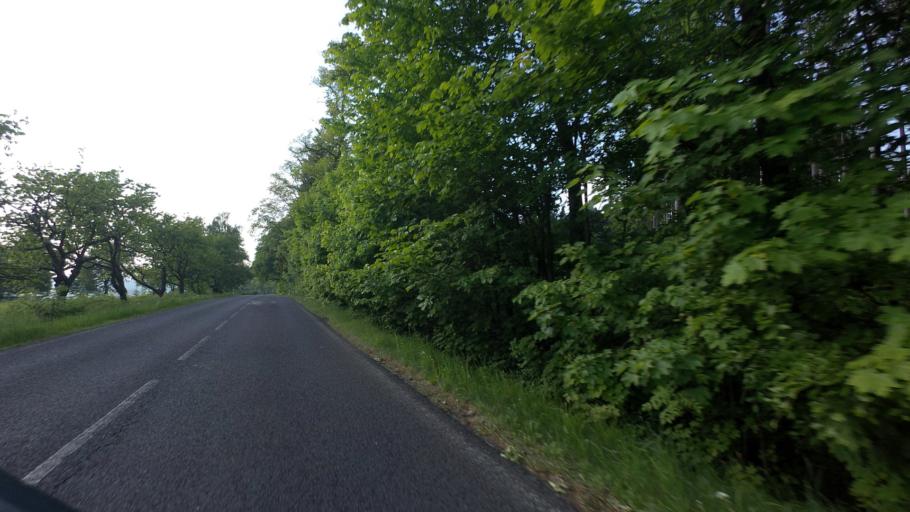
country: CZ
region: Ustecky
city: Velky Senov
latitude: 51.0067
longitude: 14.3782
